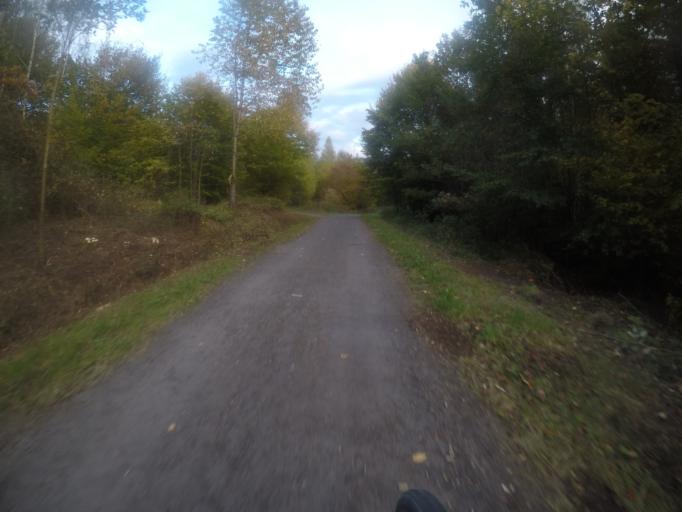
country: DE
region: Baden-Wuerttemberg
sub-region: Regierungsbezirk Stuttgart
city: Schonaich
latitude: 48.6750
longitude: 9.0440
